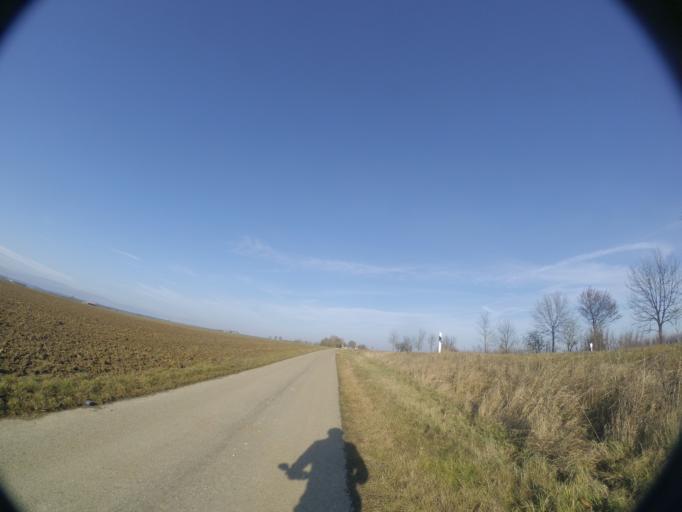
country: DE
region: Baden-Wuerttemberg
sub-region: Tuebingen Region
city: Dornstadt
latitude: 48.4805
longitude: 9.9333
